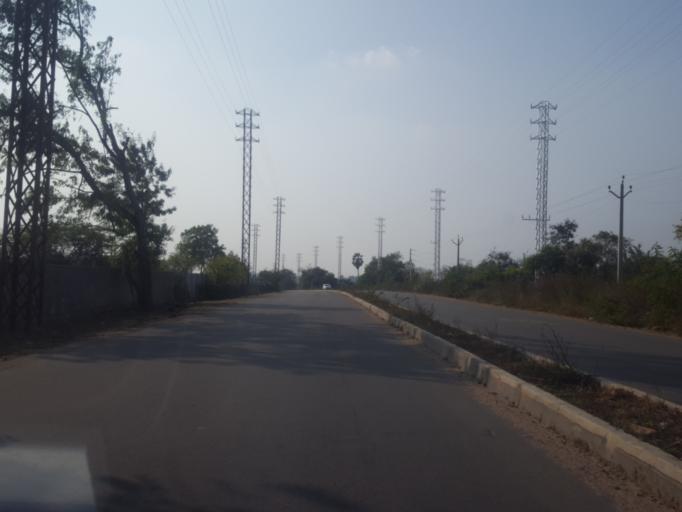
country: IN
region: Telangana
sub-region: Medak
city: Serilingampalle
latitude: 17.4181
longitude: 78.2482
